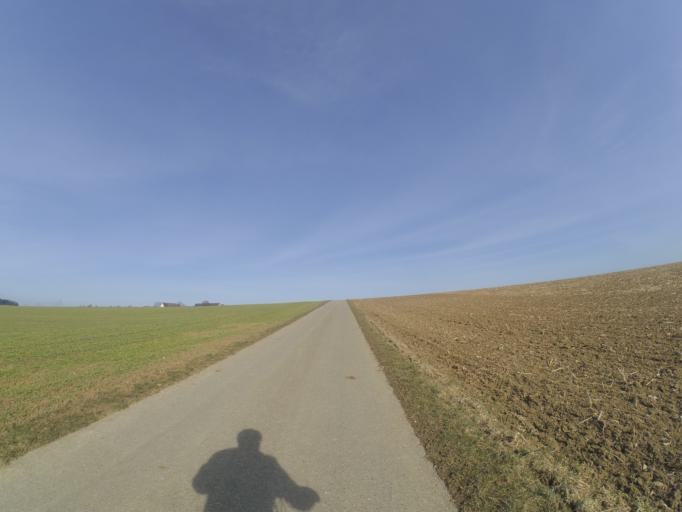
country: DE
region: Baden-Wuerttemberg
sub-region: Tuebingen Region
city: Beimerstetten
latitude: 48.4655
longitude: 9.9969
